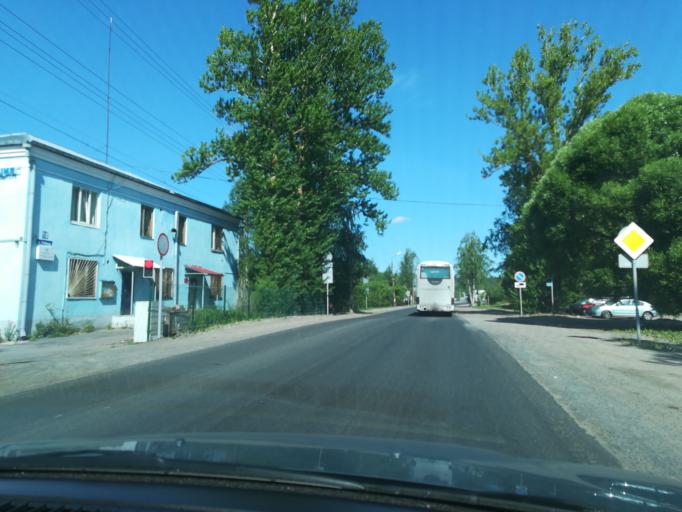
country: RU
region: Leningrad
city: Svetogorsk
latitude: 61.1151
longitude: 28.8527
